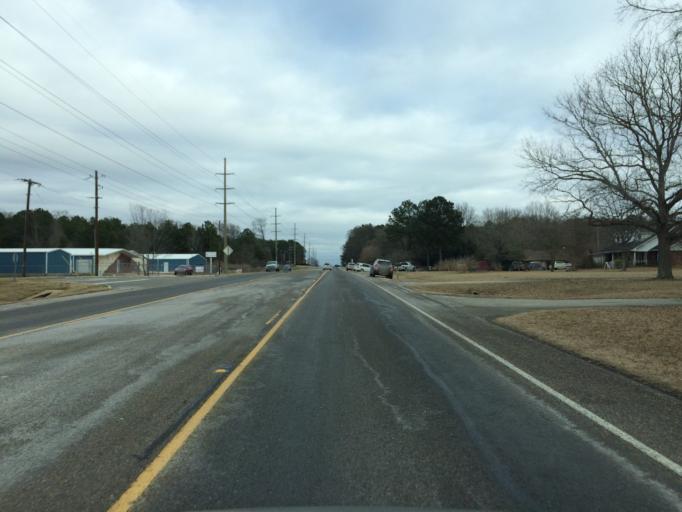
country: US
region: Texas
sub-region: Wood County
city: Mineola
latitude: 32.6880
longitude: -95.4819
